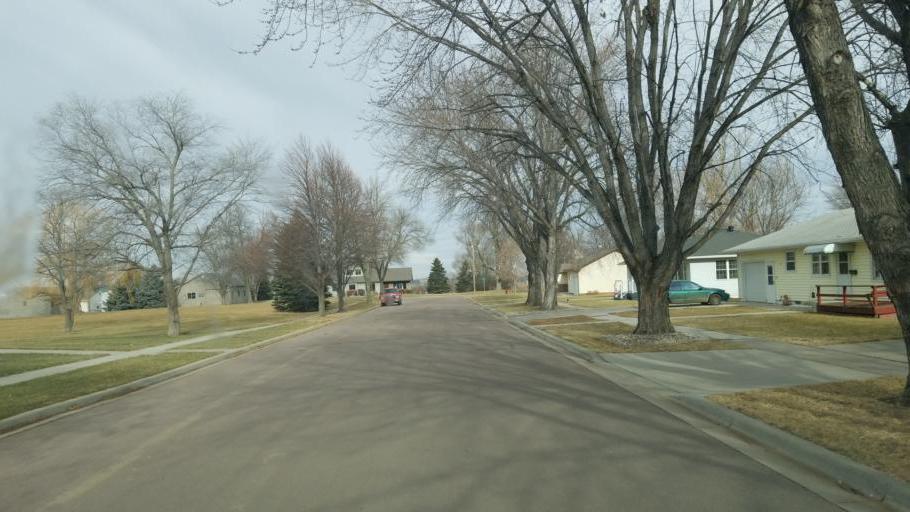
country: US
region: South Dakota
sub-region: Bon Homme County
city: Tyndall
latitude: 43.0078
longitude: -98.0586
